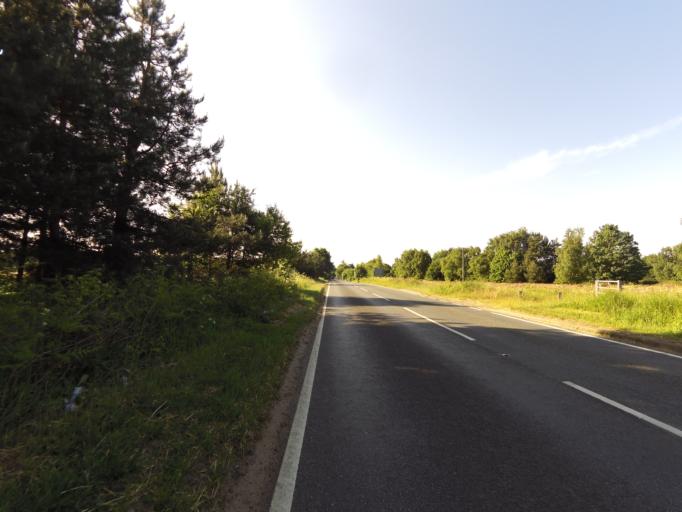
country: GB
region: England
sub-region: Suffolk
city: Woodbridge
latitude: 52.0925
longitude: 1.3522
